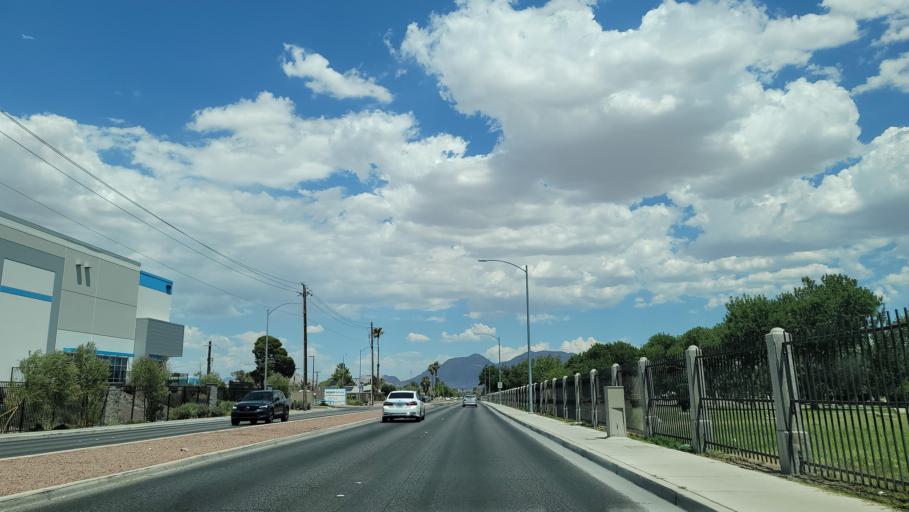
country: US
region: Nevada
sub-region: Clark County
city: Las Vegas
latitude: 36.1884
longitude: -115.1322
